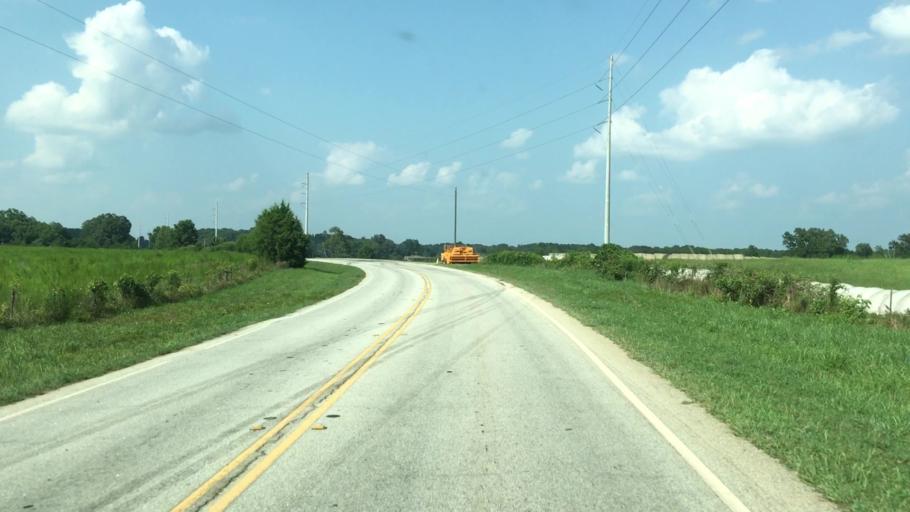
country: US
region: Georgia
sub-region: Newton County
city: Covington
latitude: 33.4972
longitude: -83.7363
